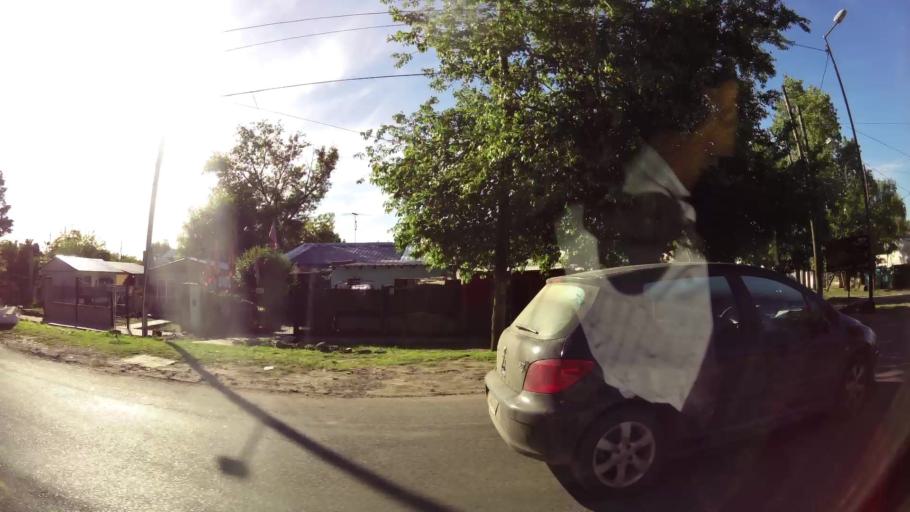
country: AR
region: Buenos Aires
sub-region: Partido de Almirante Brown
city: Adrogue
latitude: -34.8139
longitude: -58.3479
